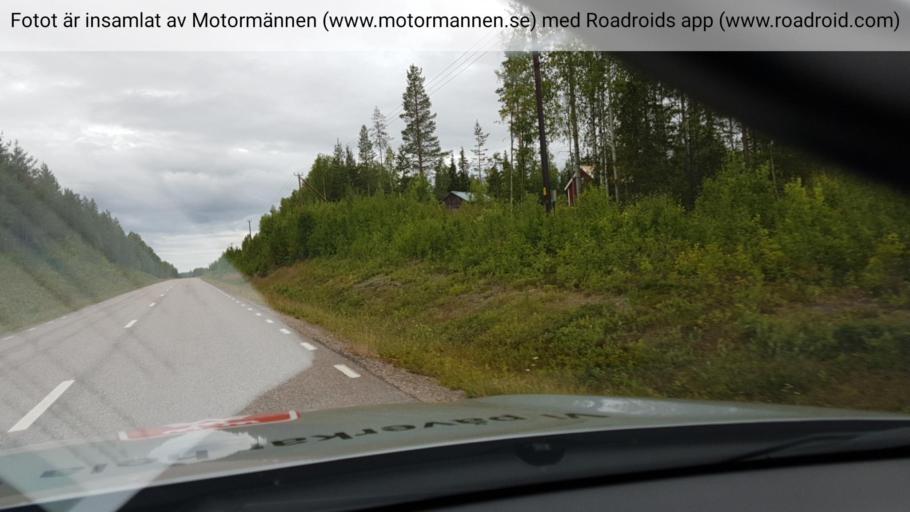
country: SE
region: Norrbotten
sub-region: Overkalix Kommun
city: OEverkalix
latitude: 66.7518
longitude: 22.9012
